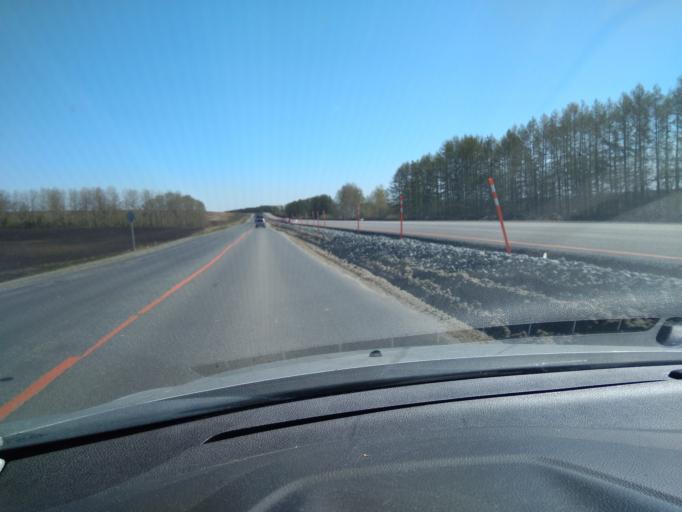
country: RU
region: Sverdlovsk
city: Kamyshlov
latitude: 56.8498
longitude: 62.8547
